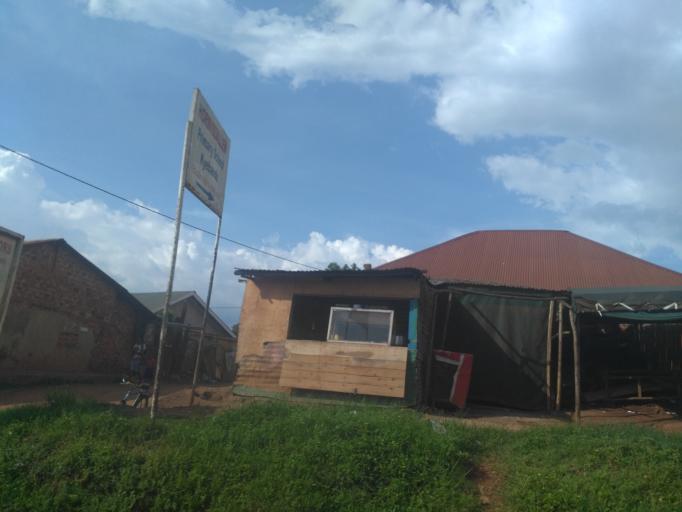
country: UG
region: Central Region
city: Kampala Central Division
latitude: 0.3603
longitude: 32.5759
